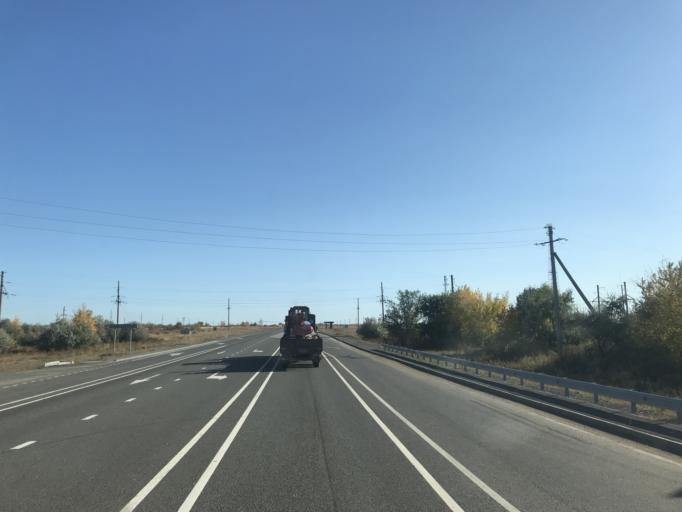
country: KZ
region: Pavlodar
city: Koktobe
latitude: 51.9259
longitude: 77.3346
